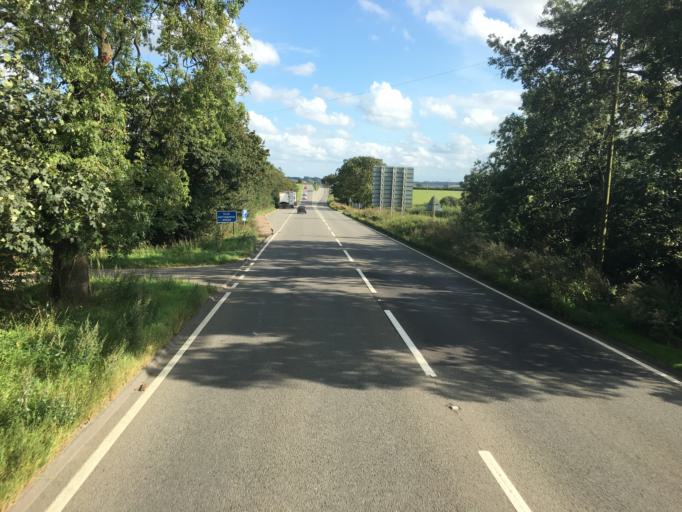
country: GB
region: England
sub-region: Leicestershire
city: Lutterworth
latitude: 52.4490
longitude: -1.2513
